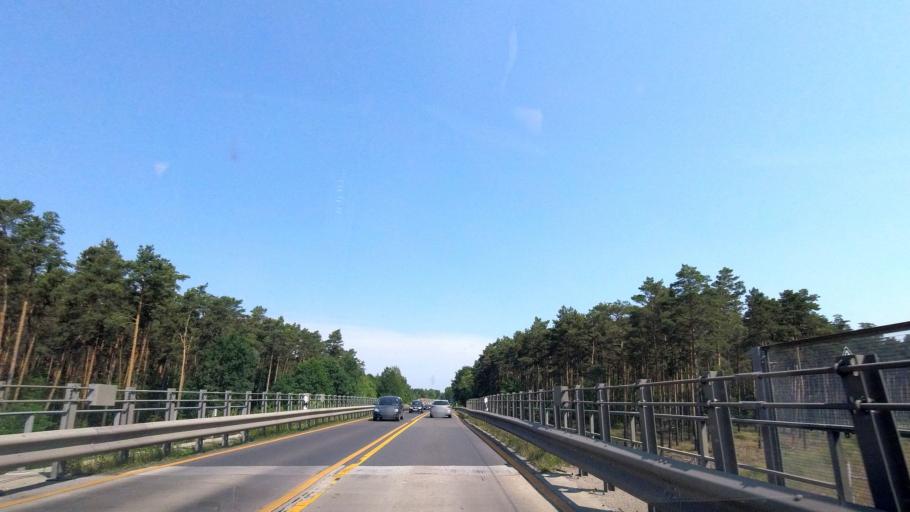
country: DE
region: Berlin
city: Bohnsdorf
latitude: 52.3845
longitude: 13.5636
